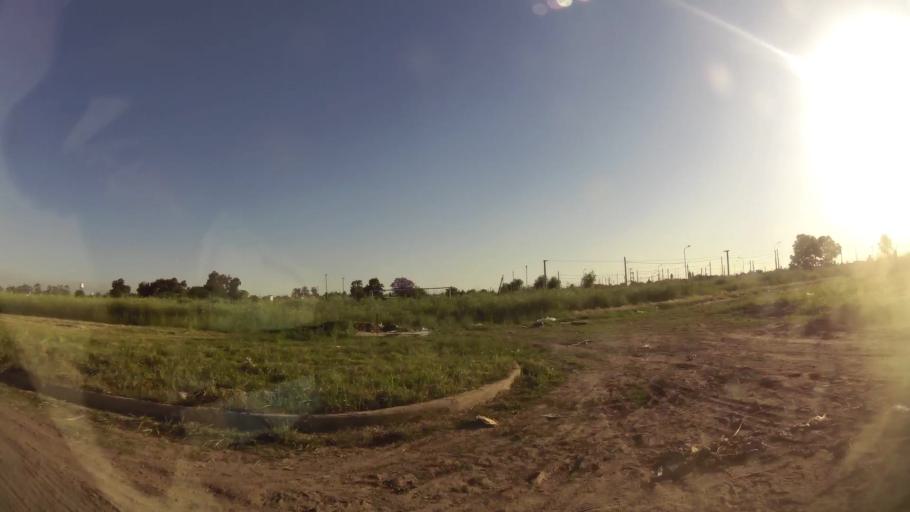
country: AR
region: Santa Fe
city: Santa Fe de la Vera Cruz
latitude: -31.5895
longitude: -60.6828
